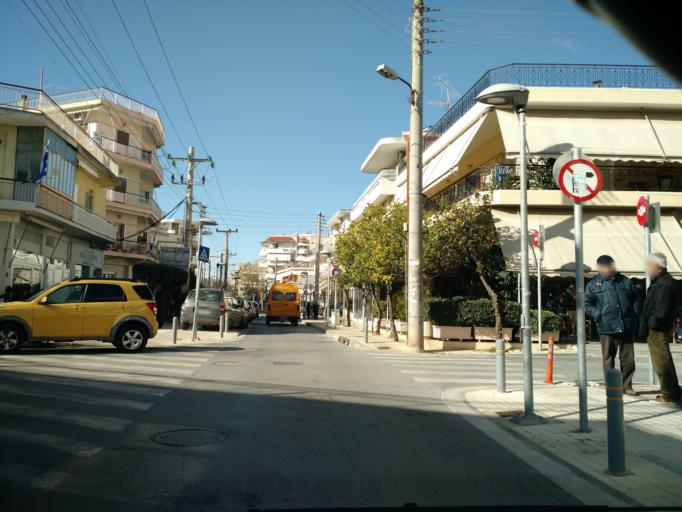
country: GR
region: Attica
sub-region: Nomarchia Athinas
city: Agia Paraskevi
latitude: 38.0191
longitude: 23.8250
